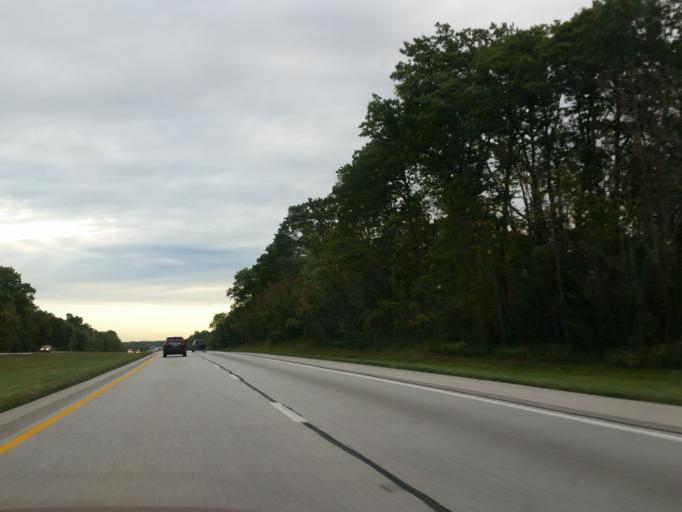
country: US
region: Ohio
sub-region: Ashtabula County
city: North Kingsville
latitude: 41.8551
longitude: -80.6953
